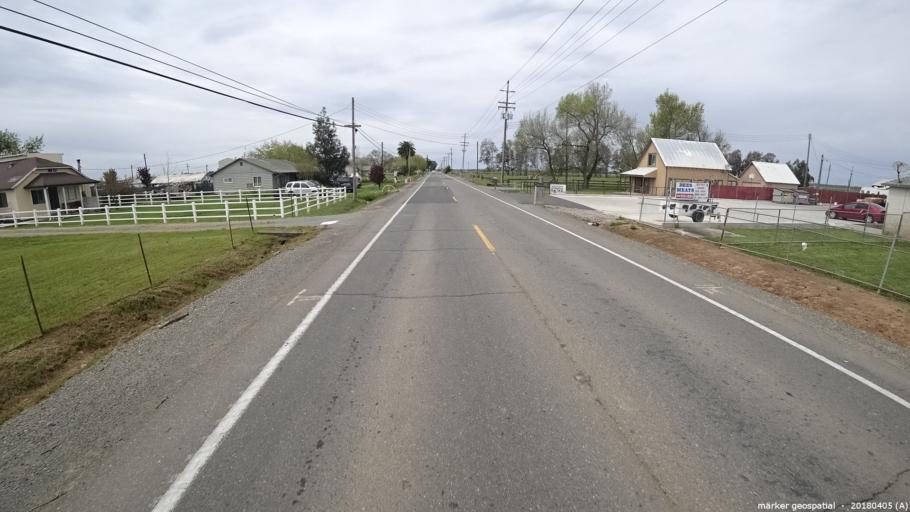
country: US
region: California
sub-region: Sacramento County
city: Galt
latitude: 38.2910
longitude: -121.3170
